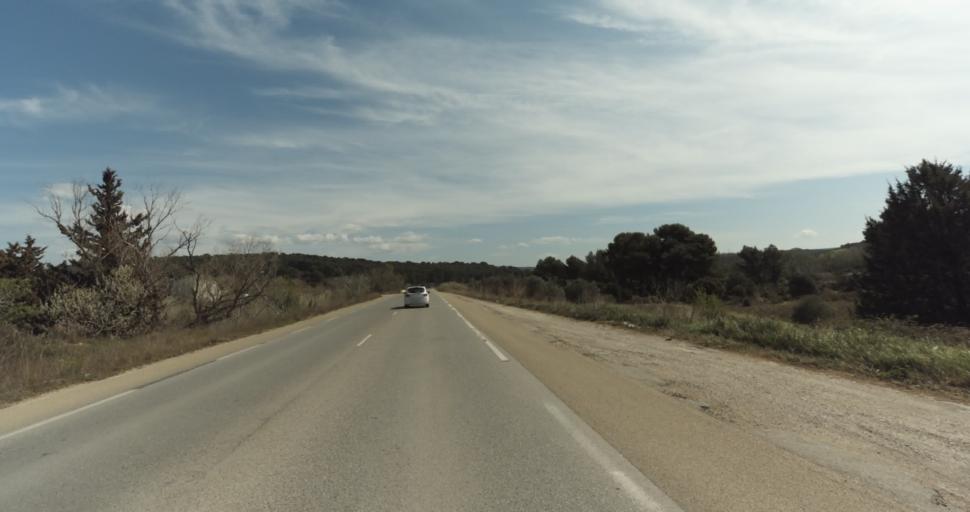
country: FR
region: Provence-Alpes-Cote d'Azur
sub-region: Departement des Bouches-du-Rhone
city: Coudoux
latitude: 43.5469
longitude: 5.2516
